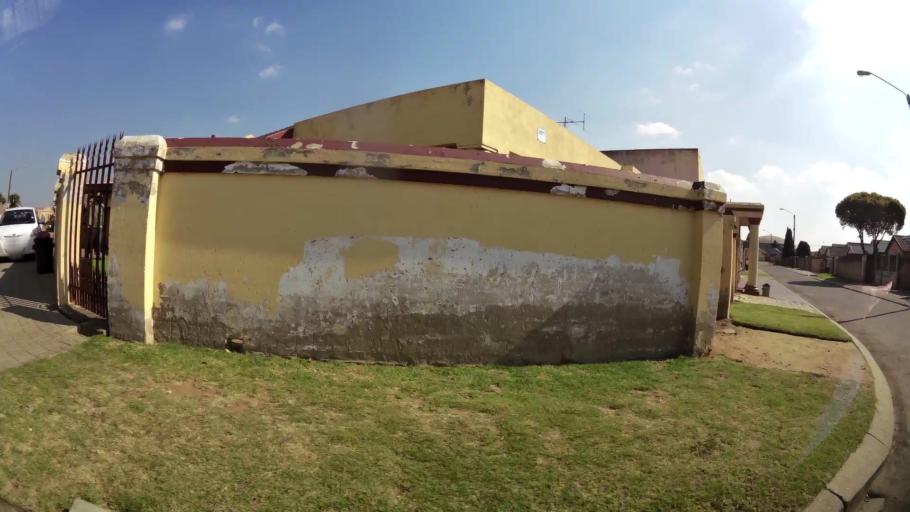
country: ZA
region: Gauteng
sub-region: Ekurhuleni Metropolitan Municipality
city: Benoni
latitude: -26.1448
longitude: 28.4043
